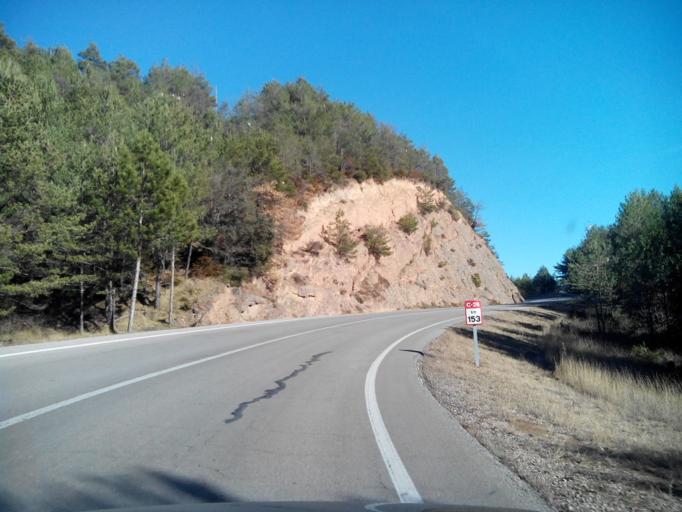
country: ES
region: Catalonia
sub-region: Provincia de Barcelona
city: Vilada
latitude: 42.1279
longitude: 1.8875
